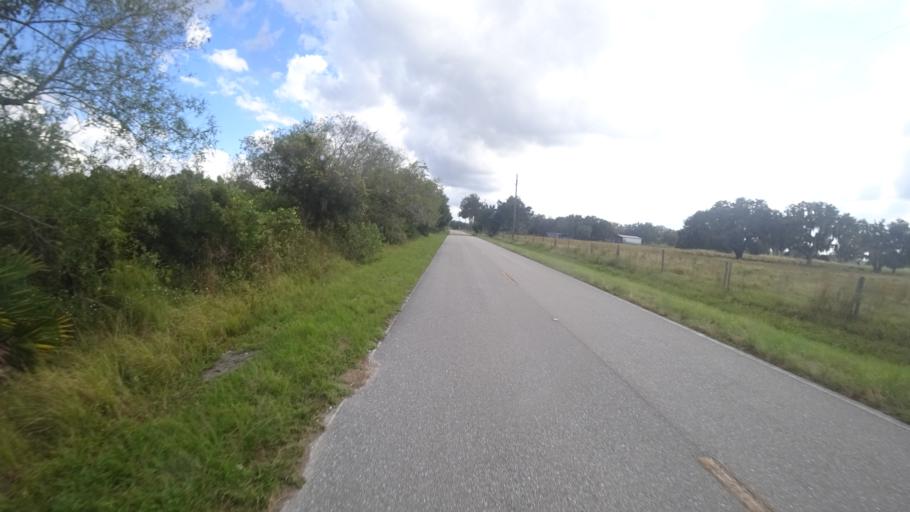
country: US
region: Florida
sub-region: Hillsborough County
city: Wimauma
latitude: 27.6075
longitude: -82.2201
